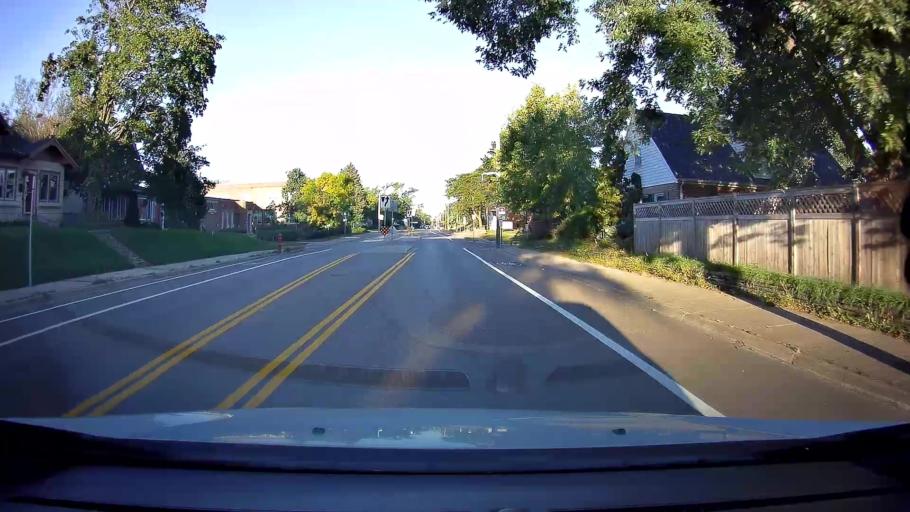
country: US
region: Minnesota
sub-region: Hennepin County
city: Richfield
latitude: 44.9197
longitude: -93.2493
